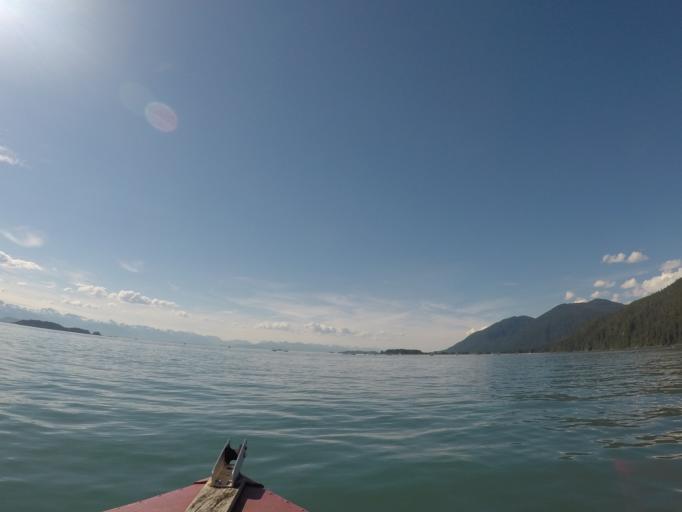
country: US
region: Alaska
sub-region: Juneau City and Borough
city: Juneau
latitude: 58.4958
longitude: -134.8185
